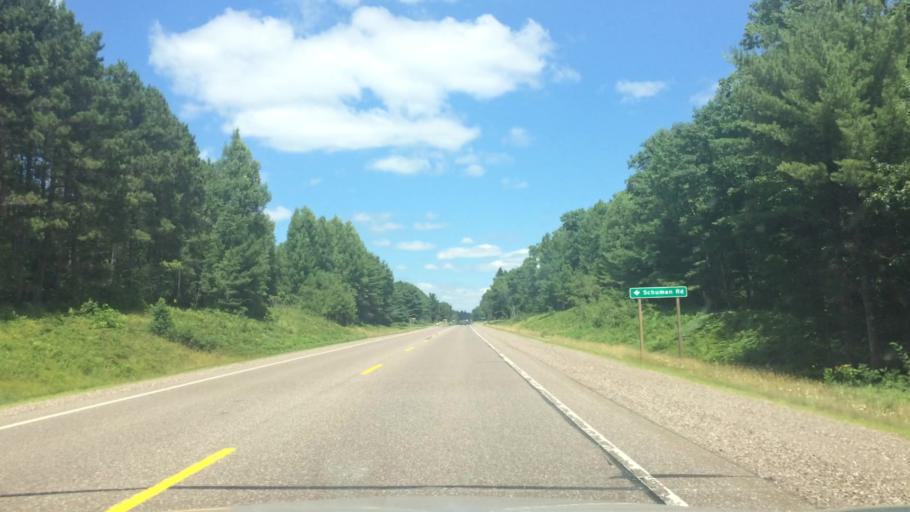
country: US
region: Wisconsin
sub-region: Vilas County
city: Lac du Flambeau
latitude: 45.9686
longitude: -89.6998
